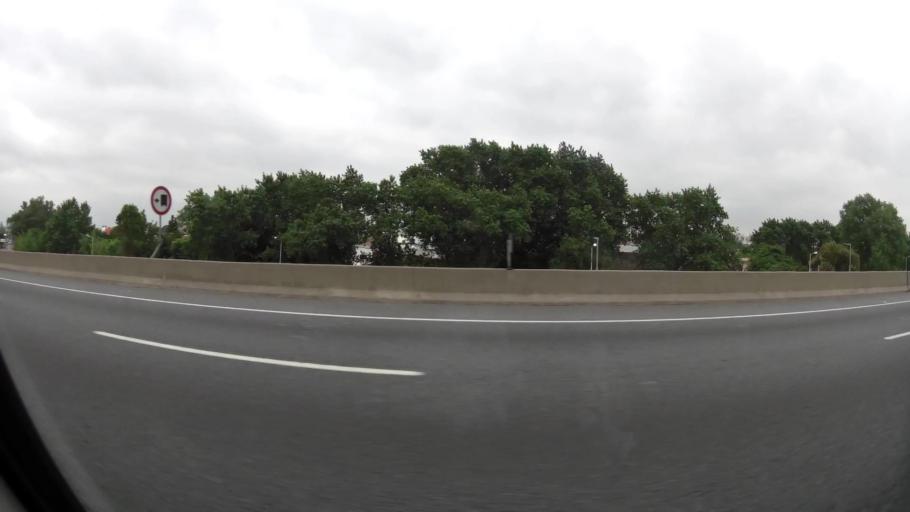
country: AR
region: Buenos Aires
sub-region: Partido de Avellaneda
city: Avellaneda
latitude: -34.6649
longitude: -58.3440
